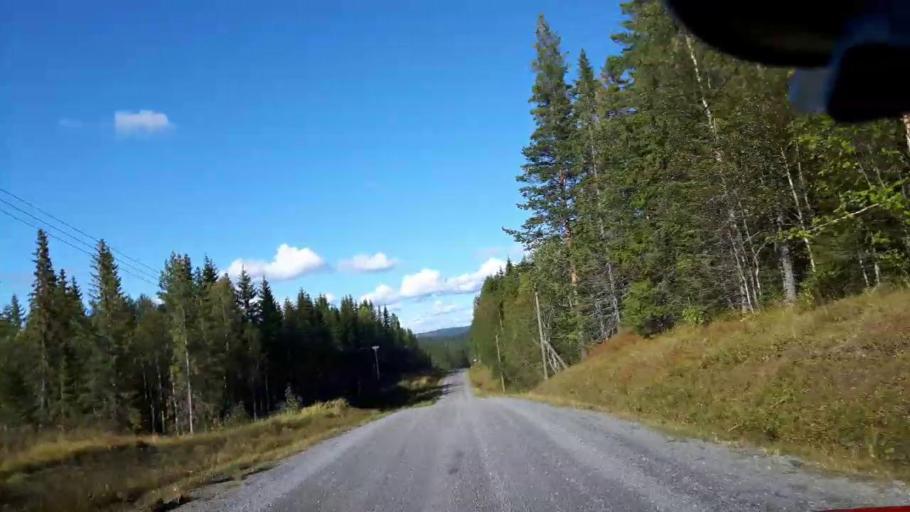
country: SE
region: Jaemtland
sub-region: Ragunda Kommun
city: Hammarstrand
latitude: 63.5087
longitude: 16.0441
